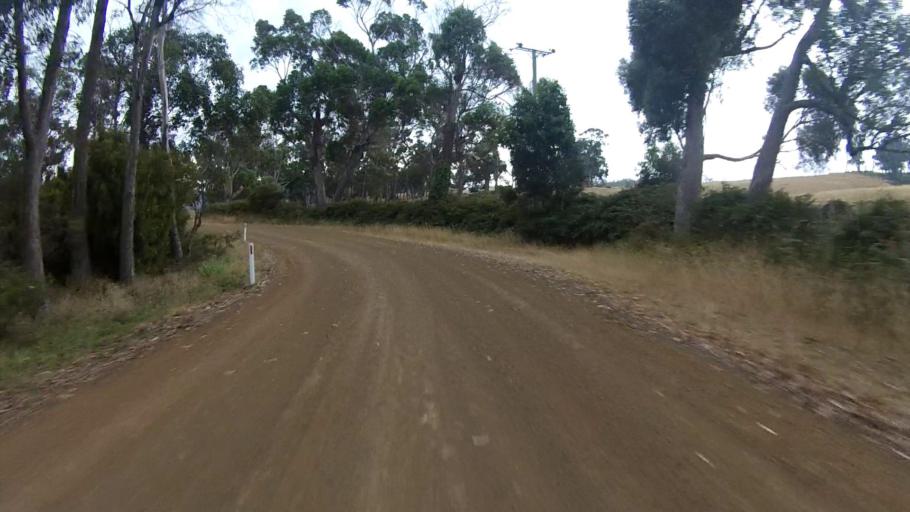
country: AU
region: Tasmania
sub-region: Huon Valley
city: Cygnet
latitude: -43.2353
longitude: 147.0991
